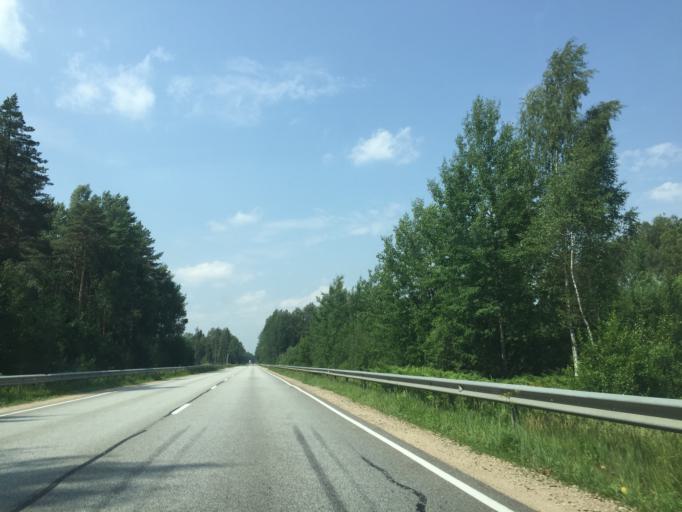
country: LV
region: Kekava
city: Balozi
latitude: 56.8185
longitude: 24.1101
